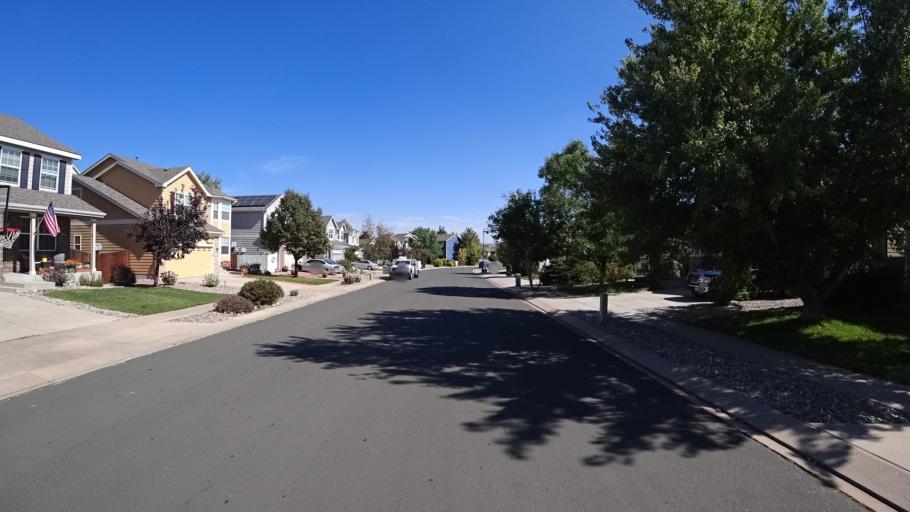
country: US
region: Colorado
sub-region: El Paso County
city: Cimarron Hills
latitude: 38.8929
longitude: -104.6952
